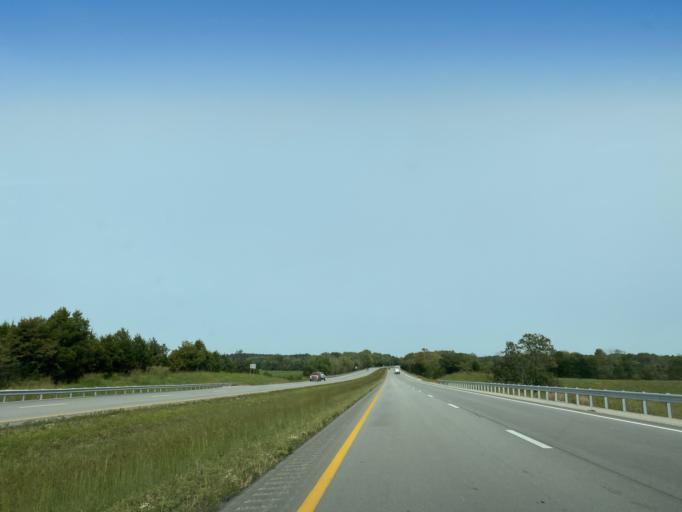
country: US
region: Kentucky
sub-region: Bullitt County
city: Lebanon Junction
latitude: 37.7418
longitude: -85.6927
